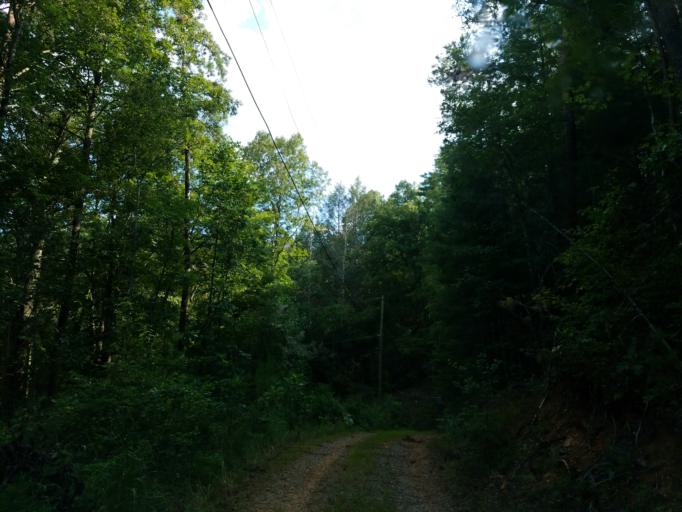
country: US
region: Georgia
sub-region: Fannin County
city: Blue Ridge
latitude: 34.7930
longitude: -84.4084
